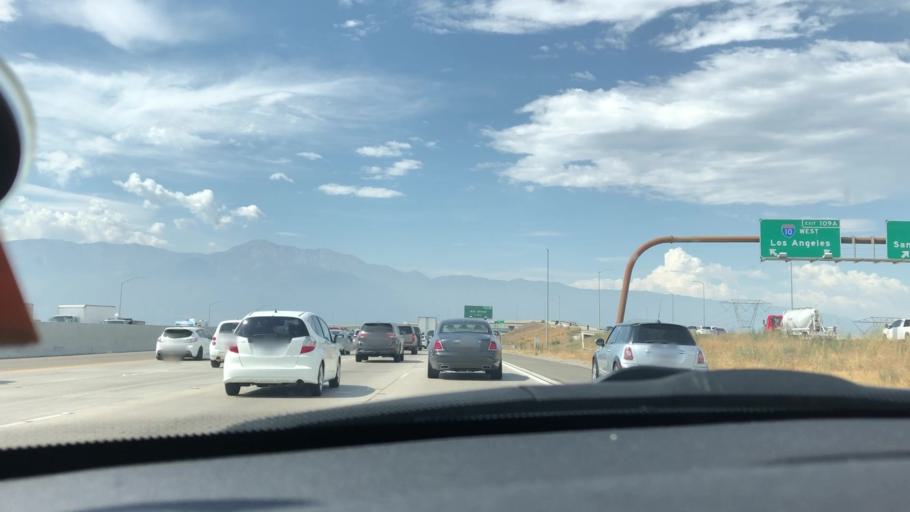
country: US
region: California
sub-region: San Bernardino County
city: Rancho Cucamonga
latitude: 34.0614
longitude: -117.5446
